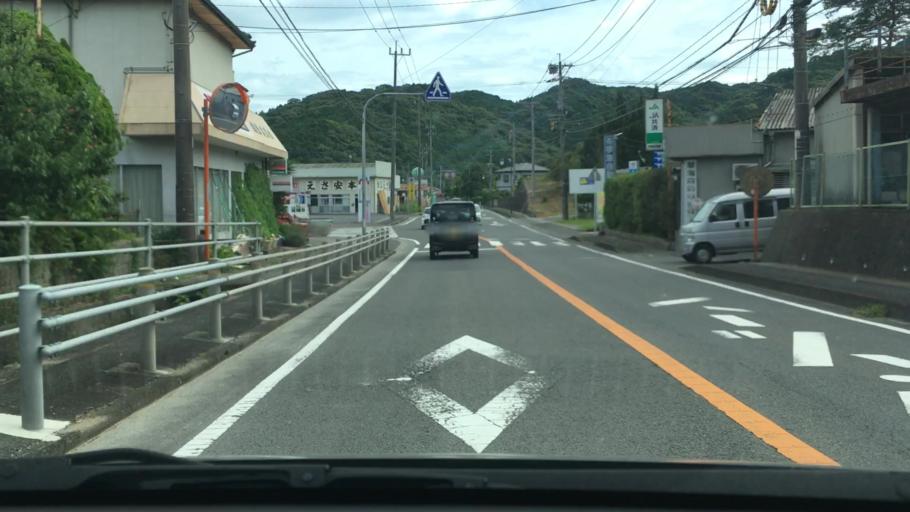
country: JP
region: Nagasaki
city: Togitsu
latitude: 32.8971
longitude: 129.7807
